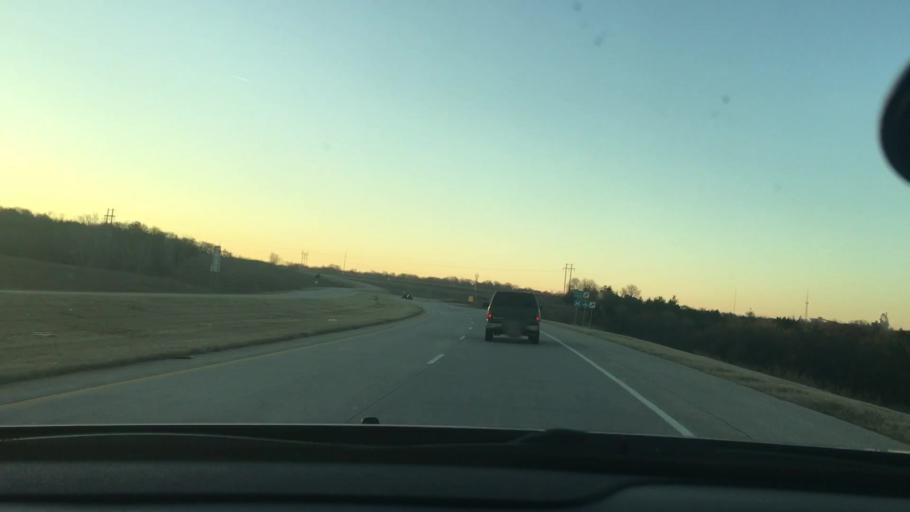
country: US
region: Oklahoma
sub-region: Pontotoc County
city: Ada
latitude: 34.7961
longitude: -96.6957
